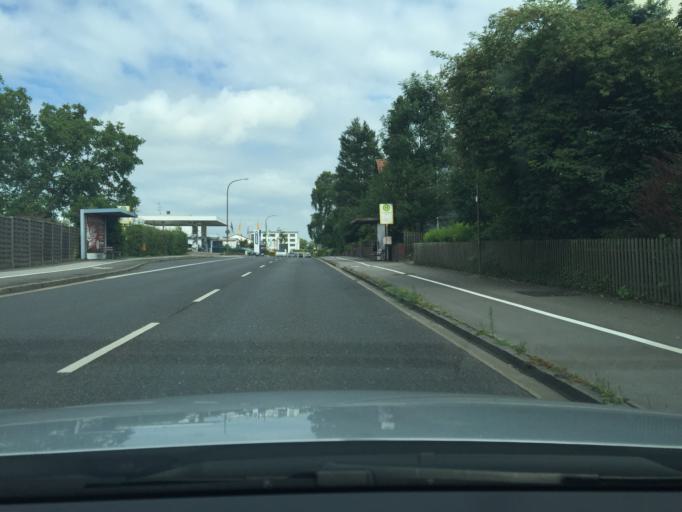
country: DE
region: North Rhine-Westphalia
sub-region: Regierungsbezirk Dusseldorf
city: Heiligenhaus
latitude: 51.3253
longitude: 6.9485
